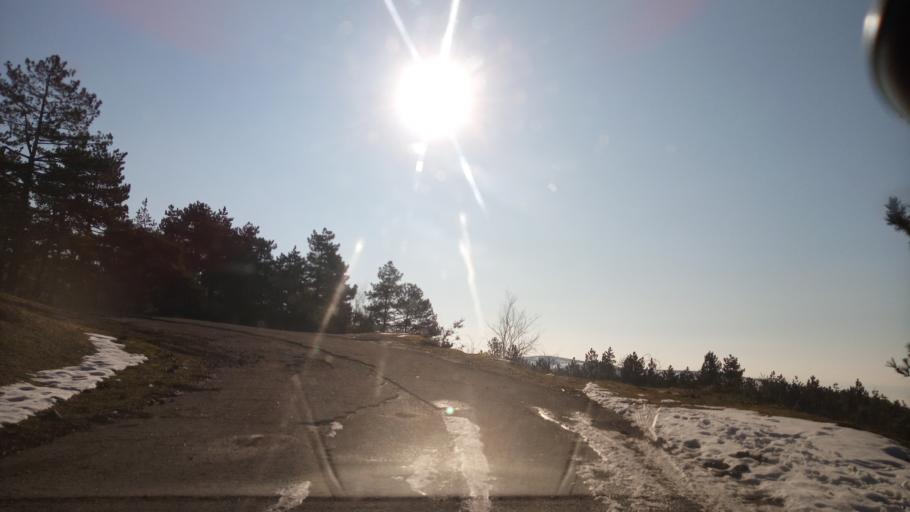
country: BG
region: Sofia-Capital
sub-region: Stolichna Obshtina
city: Bukhovo
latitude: 42.7949
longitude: 23.5315
